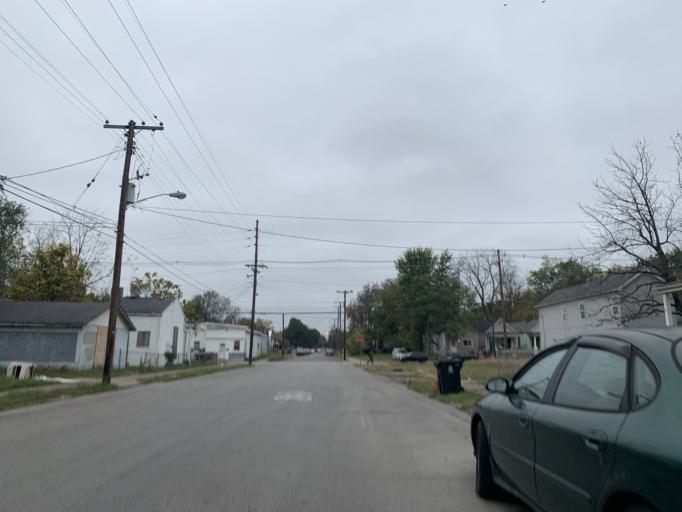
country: US
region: Kentucky
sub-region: Jefferson County
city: Louisville
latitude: 38.2621
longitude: -85.7927
